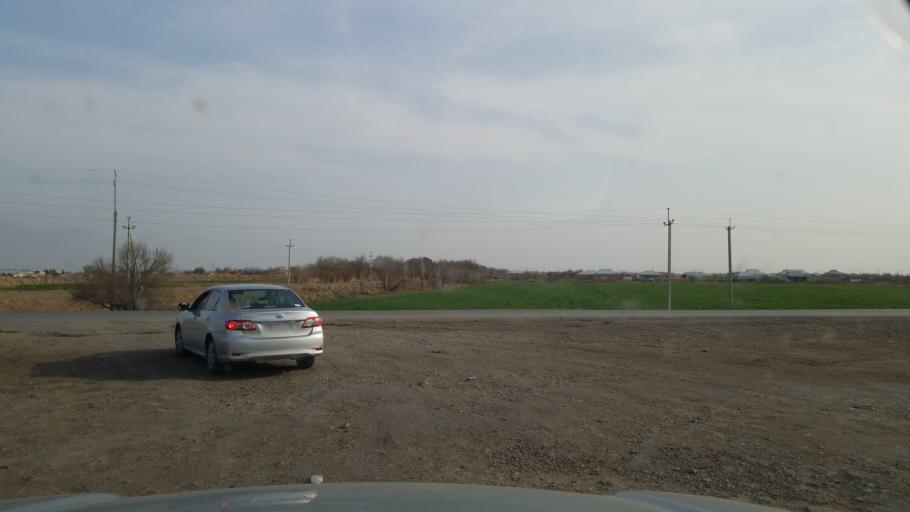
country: TM
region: Mary
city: Bayramaly
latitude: 37.6090
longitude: 62.2537
